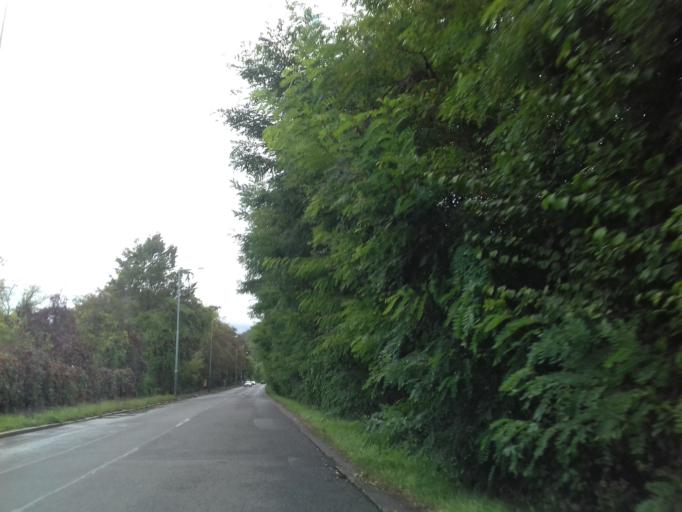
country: CZ
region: Praha
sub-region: Praha 12
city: Modrany
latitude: 50.0047
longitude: 14.3862
